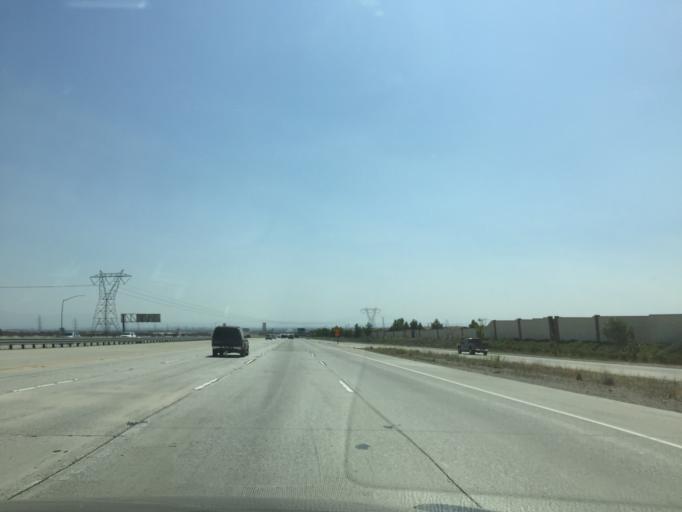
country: US
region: California
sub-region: San Bernardino County
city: Fontana
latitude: 34.1631
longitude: -117.4641
